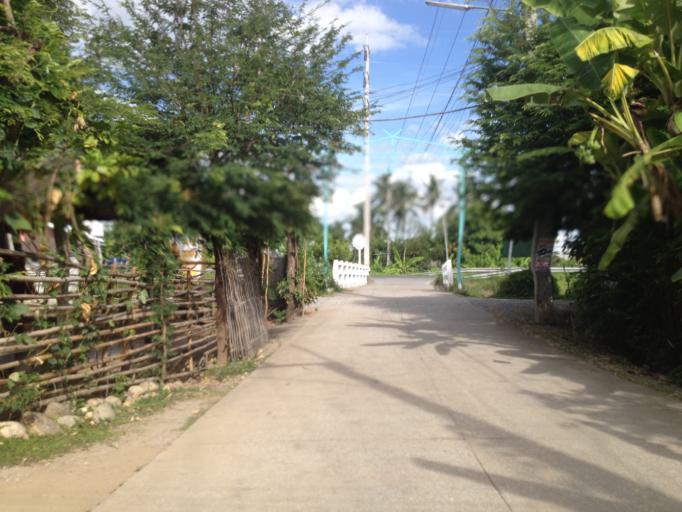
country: TH
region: Chiang Mai
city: Hang Dong
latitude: 18.7110
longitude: 98.9239
